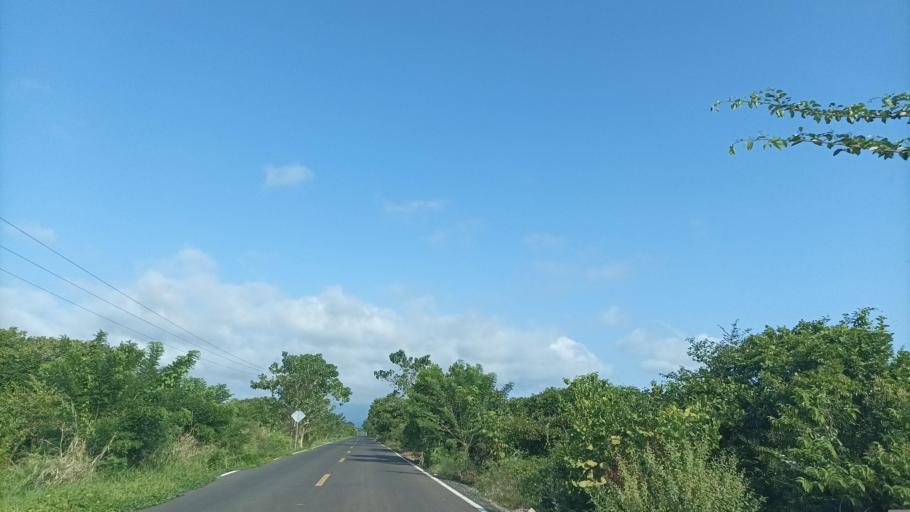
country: MX
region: Veracruz
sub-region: Chinameca
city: Chacalapa
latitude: 18.1479
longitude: -94.6541
